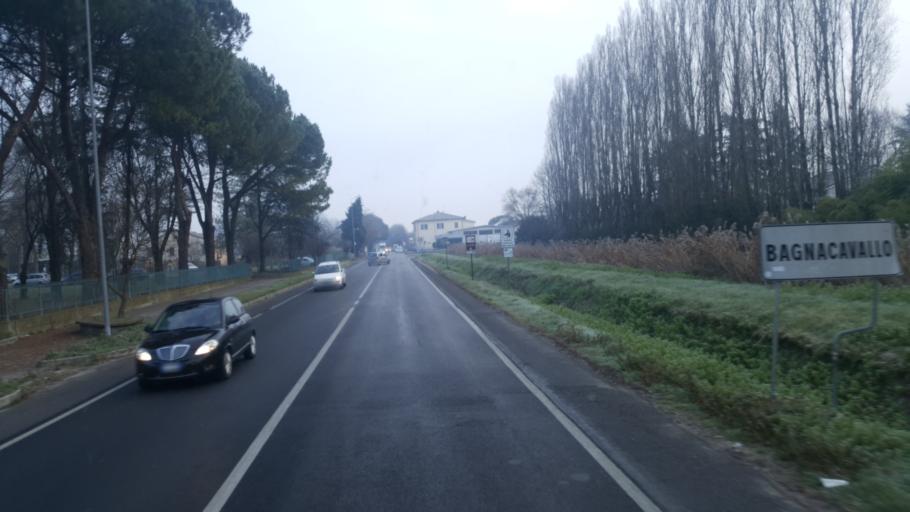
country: IT
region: Emilia-Romagna
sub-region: Provincia di Ravenna
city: Bagnacavallo
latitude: 44.4075
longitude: 11.9681
